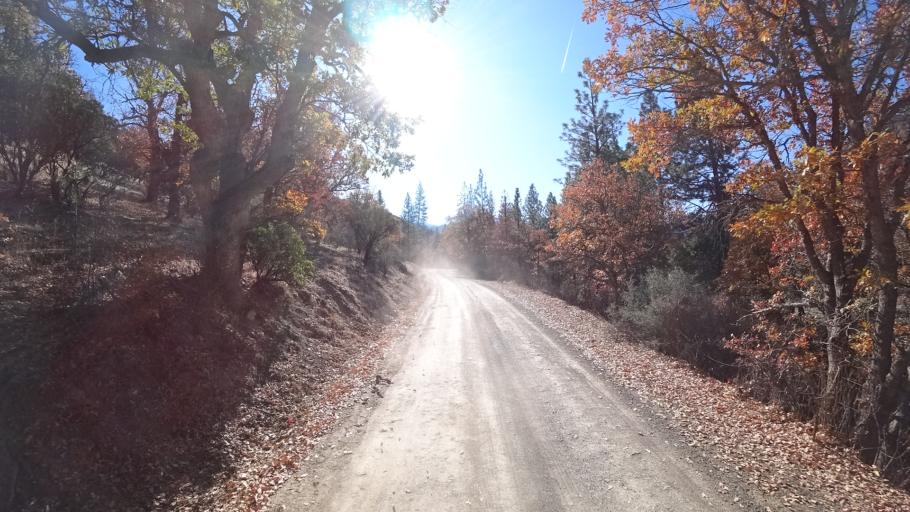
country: US
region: California
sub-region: Siskiyou County
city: Yreka
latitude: 41.8437
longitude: -122.8371
